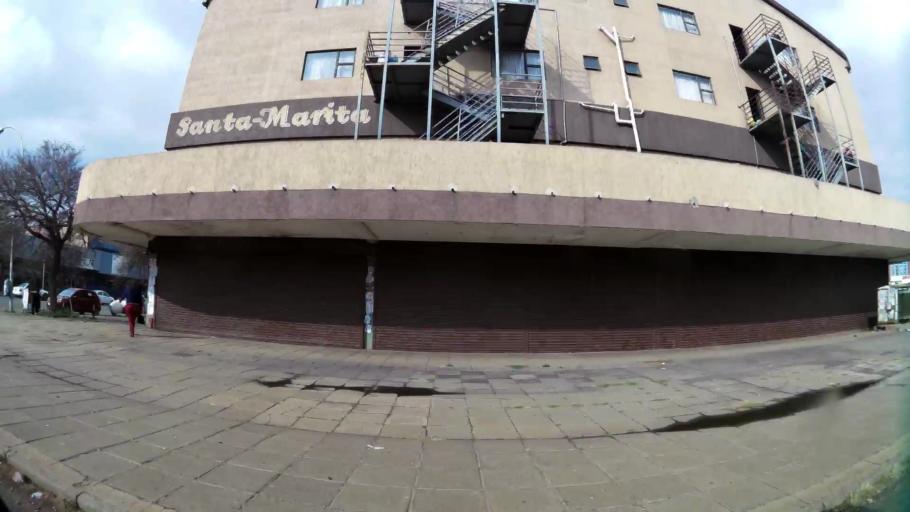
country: ZA
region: Gauteng
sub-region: Sedibeng District Municipality
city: Vanderbijlpark
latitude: -26.6956
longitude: 27.8350
